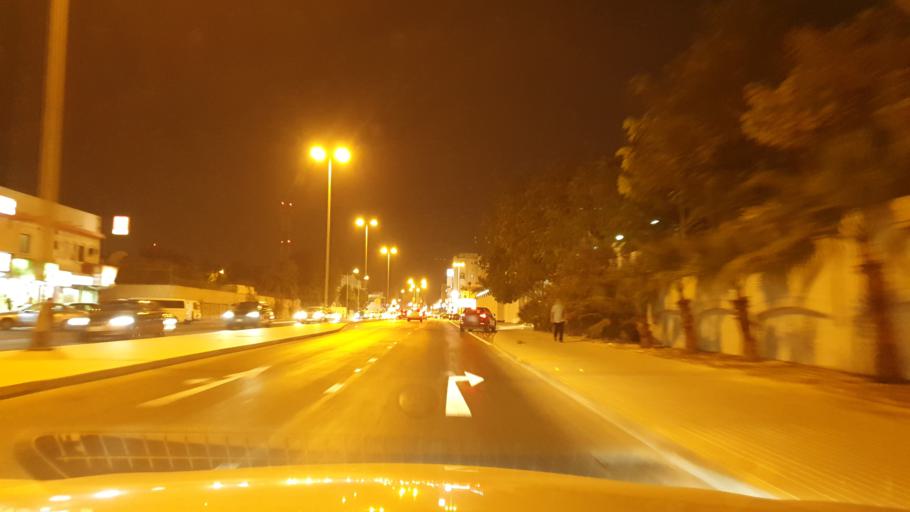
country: BH
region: Manama
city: Jidd Hafs
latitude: 26.1981
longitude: 50.4855
